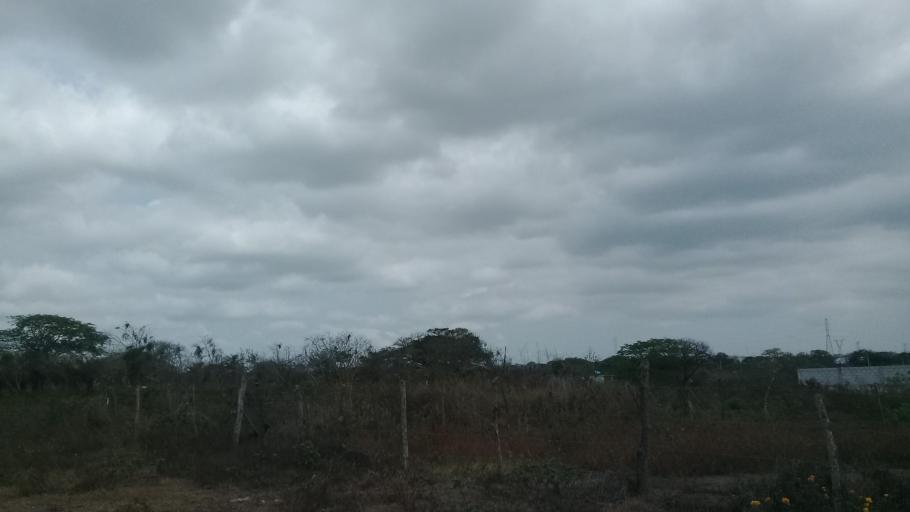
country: MX
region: Veracruz
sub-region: Veracruz
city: Las Amapolas
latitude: 19.1318
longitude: -96.2369
